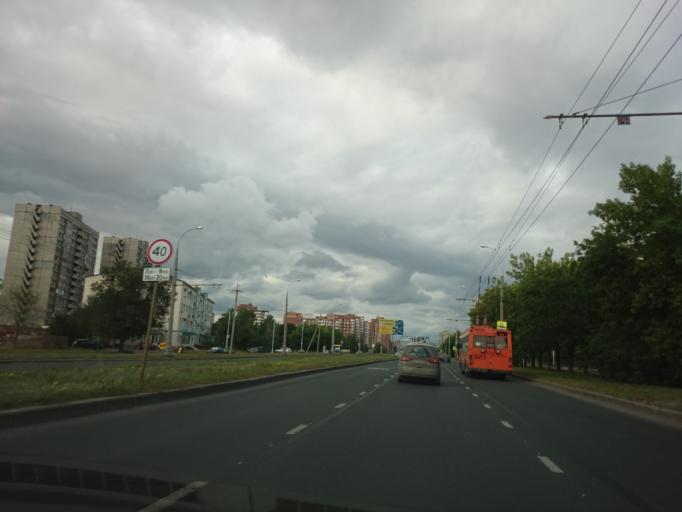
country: RU
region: Samara
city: Tol'yatti
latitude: 53.5096
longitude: 49.3038
